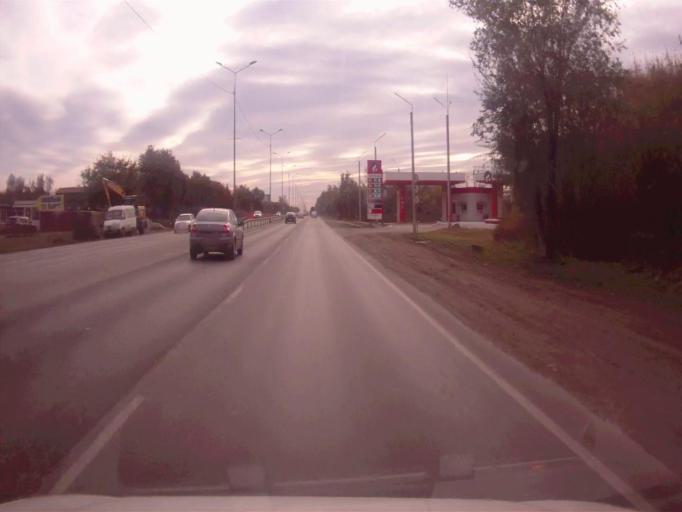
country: RU
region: Chelyabinsk
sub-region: Gorod Chelyabinsk
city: Chelyabinsk
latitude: 55.1073
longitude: 61.4079
